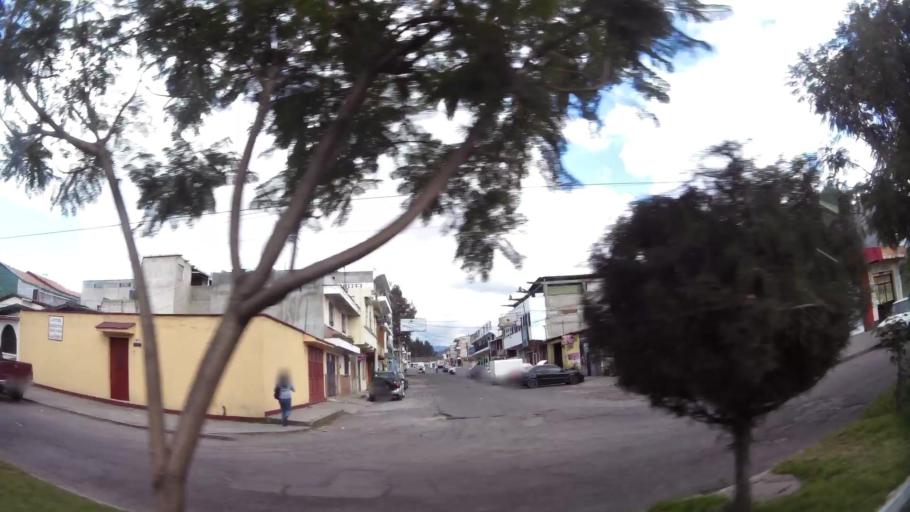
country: GT
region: Quetzaltenango
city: Quetzaltenango
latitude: 14.8413
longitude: -91.5256
